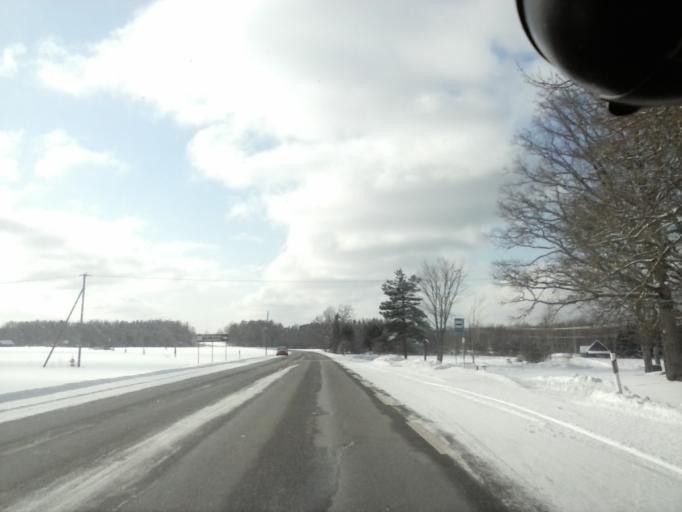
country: EE
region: Paernumaa
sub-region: Saarde vald
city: Kilingi-Nomme
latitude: 58.1773
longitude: 25.0413
